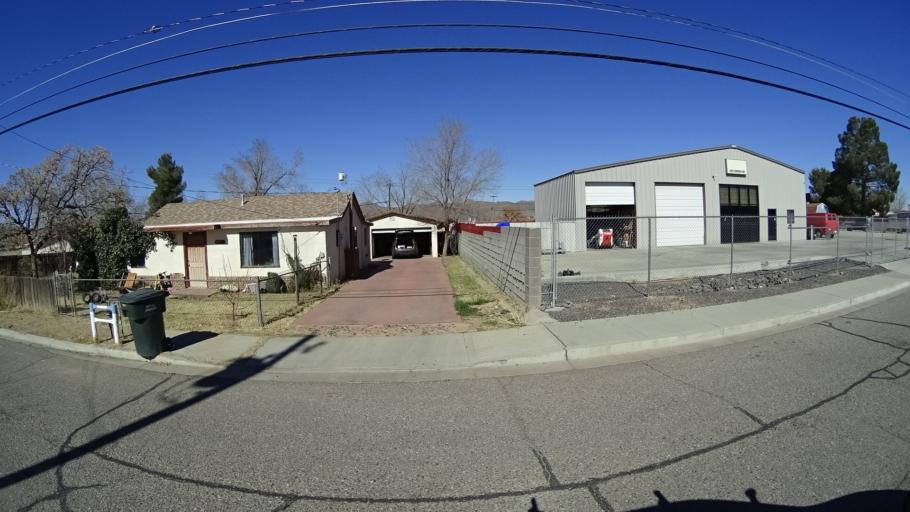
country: US
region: Arizona
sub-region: Mohave County
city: Kingman
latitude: 35.2038
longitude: -114.0242
